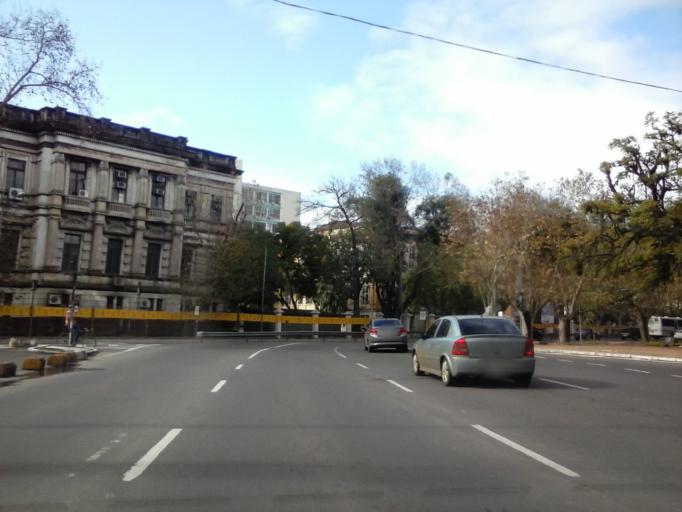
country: BR
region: Rio Grande do Sul
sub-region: Porto Alegre
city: Porto Alegre
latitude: -30.0346
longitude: -51.2209
